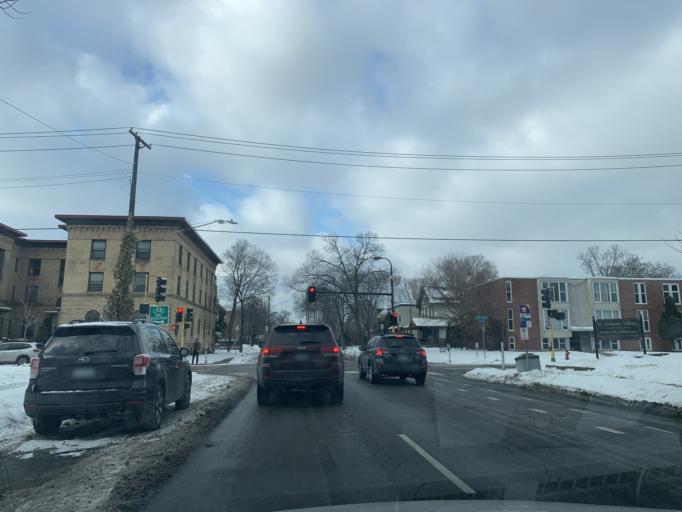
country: US
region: Minnesota
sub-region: Hennepin County
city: Minneapolis
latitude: 44.9847
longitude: -93.2465
